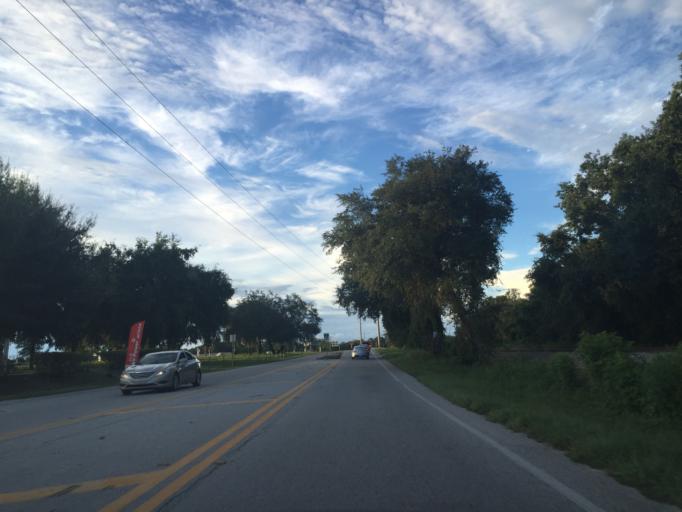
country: US
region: Florida
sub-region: Lake County
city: Tavares
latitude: 28.7830
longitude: -81.7478
